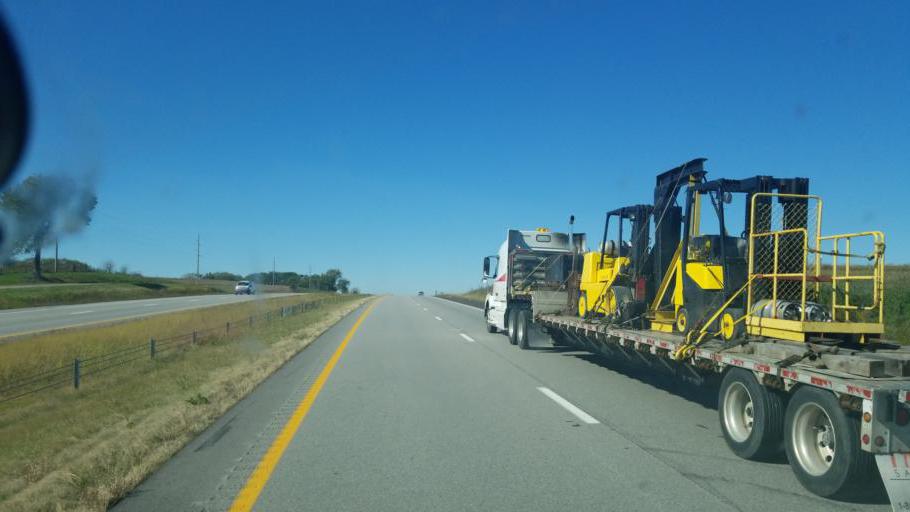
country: US
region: Missouri
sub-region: Lafayette County
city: Concordia
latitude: 38.9916
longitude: -93.6119
